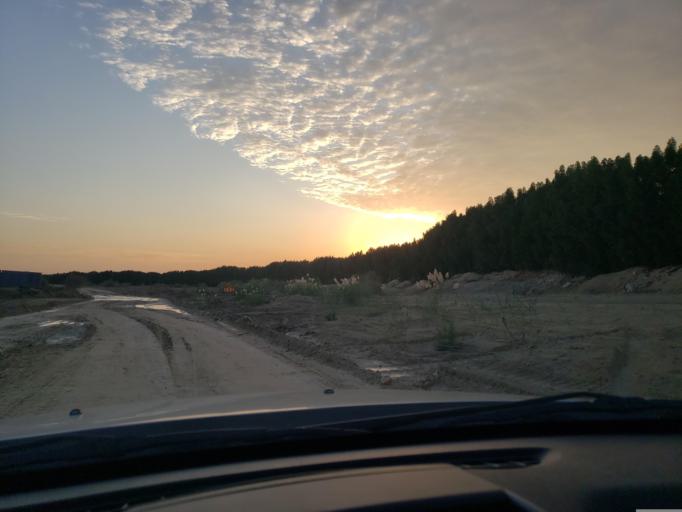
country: AE
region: Dubai
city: Dubai
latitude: 25.0210
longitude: 55.2636
